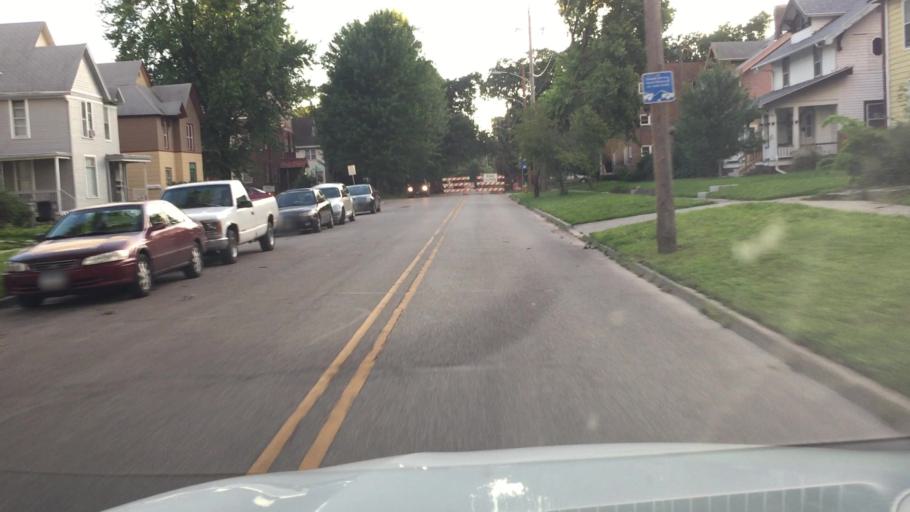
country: US
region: Iowa
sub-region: Polk County
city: Des Moines
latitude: 41.5986
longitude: -93.6560
